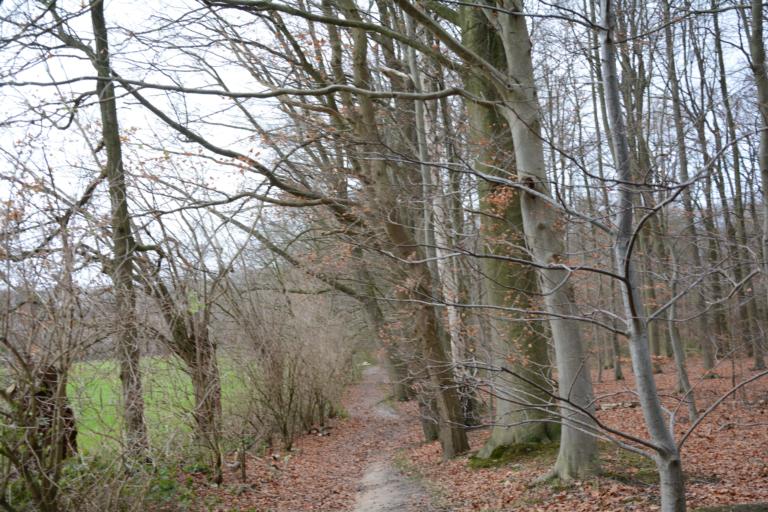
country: BE
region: Flanders
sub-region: Provincie Vlaams-Brabant
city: Opwijk
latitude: 50.9348
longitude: 4.1592
